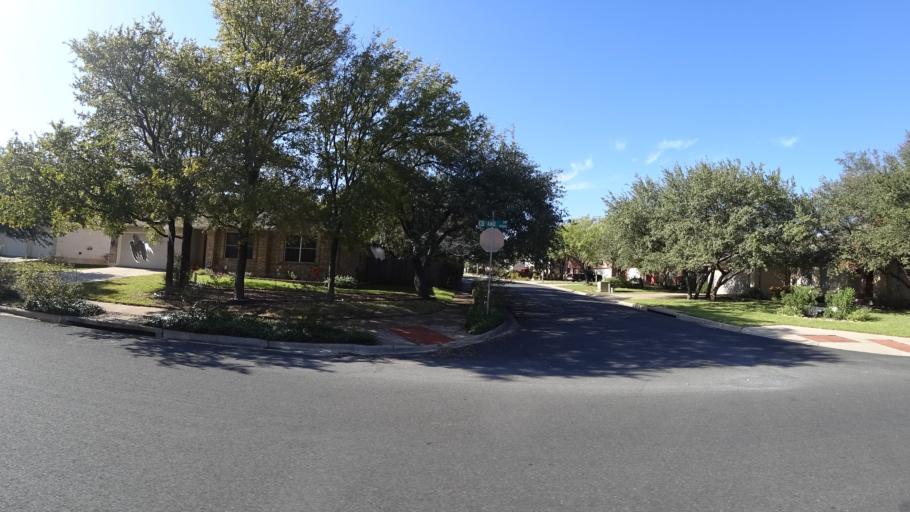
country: US
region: Texas
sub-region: Travis County
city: Shady Hollow
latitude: 30.2049
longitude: -97.8538
